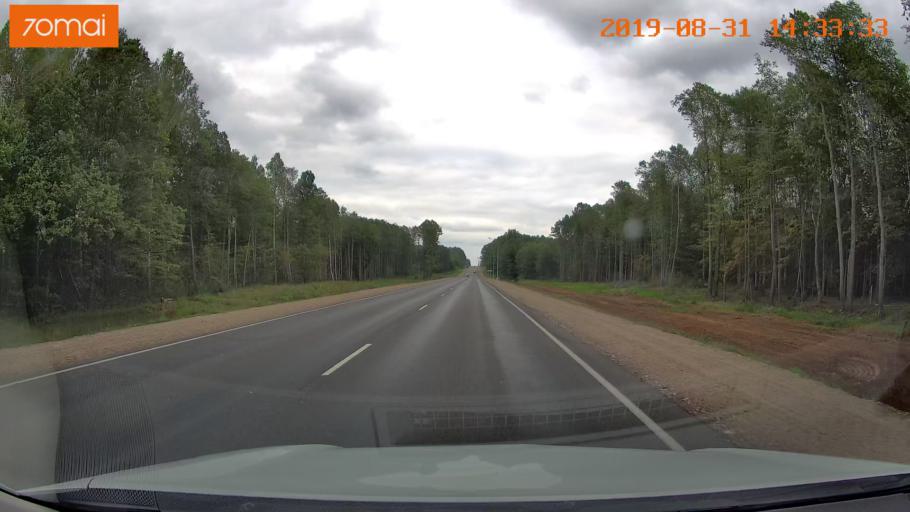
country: RU
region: Smolensk
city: Yekimovichi
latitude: 54.1525
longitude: 33.4212
